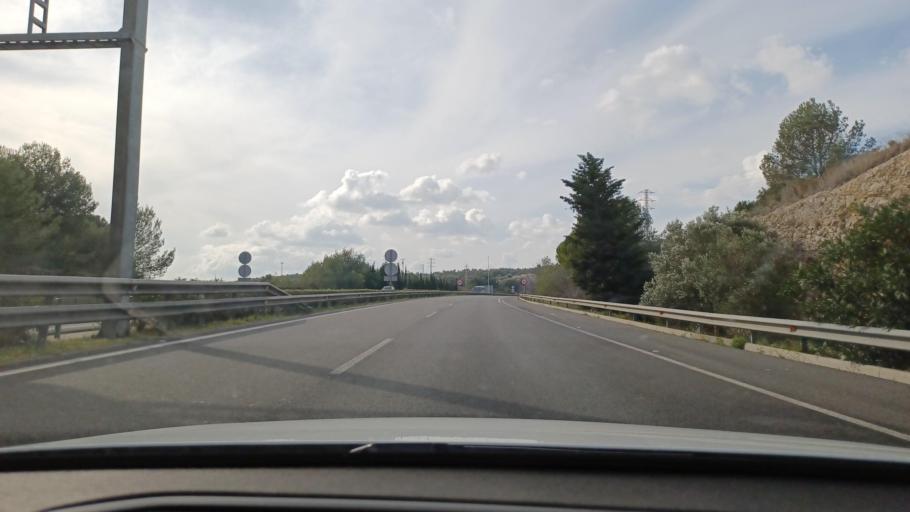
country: ES
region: Catalonia
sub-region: Provincia de Tarragona
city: Cunit
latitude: 41.2093
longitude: 1.6464
